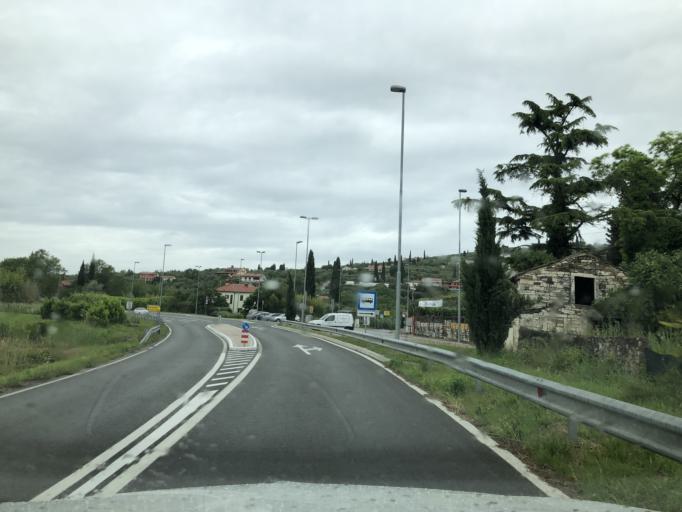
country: SI
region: Piran-Pirano
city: Seca
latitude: 45.4824
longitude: 13.6235
